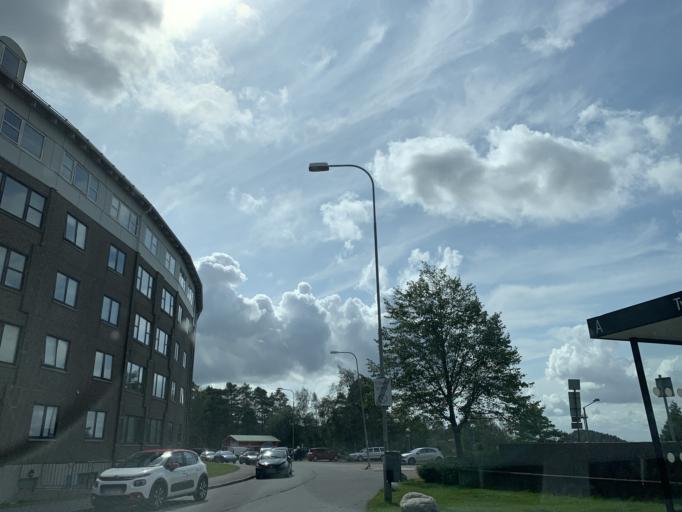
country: SE
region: Vaestra Goetaland
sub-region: Goteborg
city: Eriksbo
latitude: 57.7626
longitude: 12.0582
